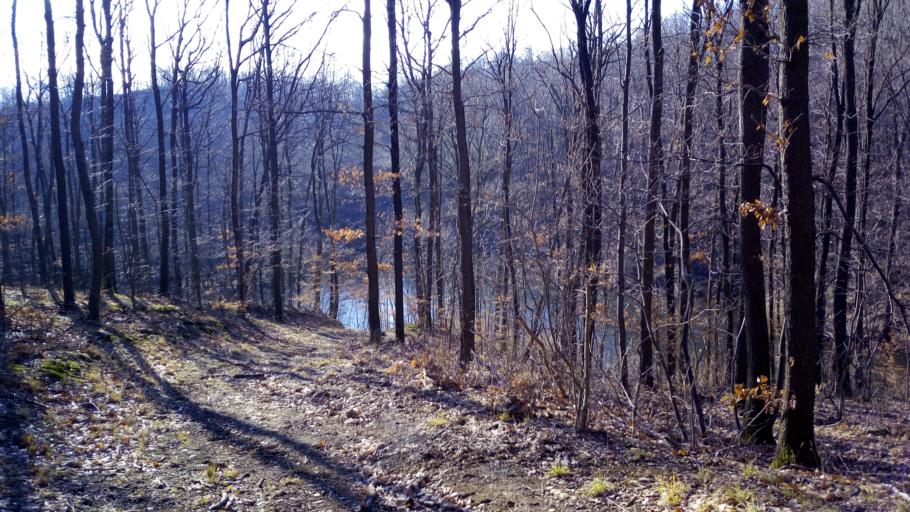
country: HU
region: Baranya
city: Pecs
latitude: 46.1152
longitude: 18.2378
